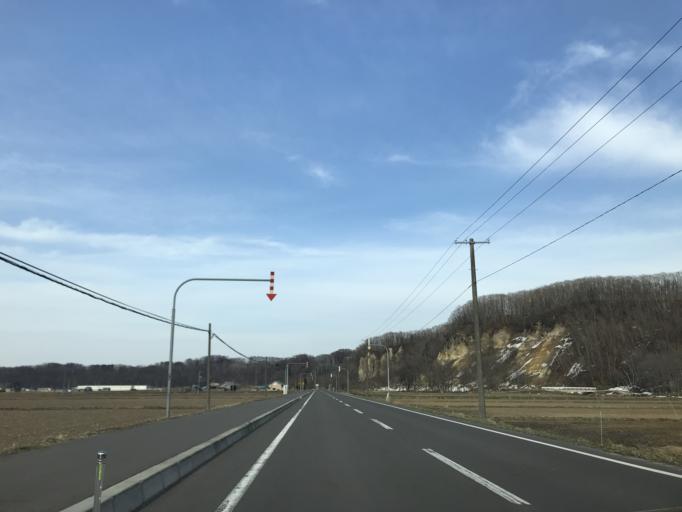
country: JP
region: Hokkaido
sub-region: Asahikawa-shi
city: Asahikawa
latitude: 43.6999
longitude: 142.3438
